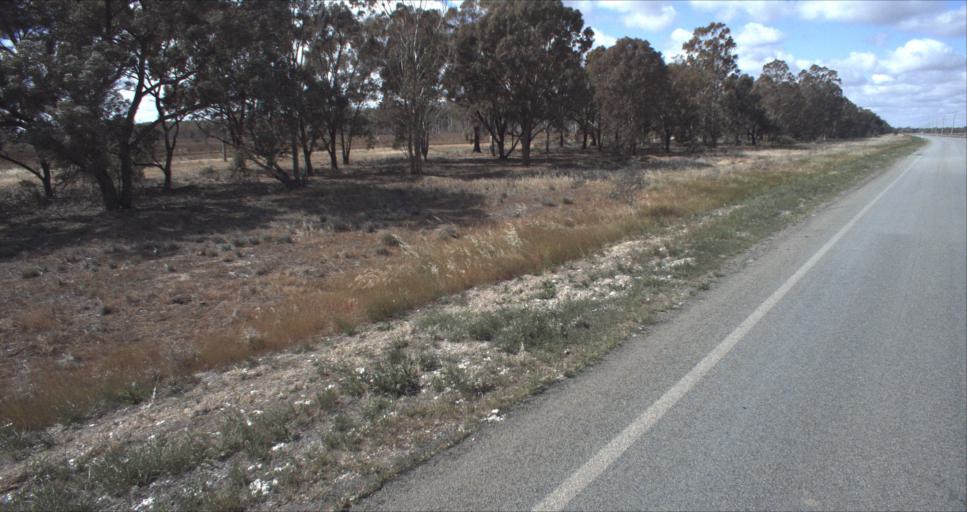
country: AU
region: New South Wales
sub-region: Murrumbidgee Shire
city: Darlington Point
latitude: -34.5785
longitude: 146.1656
